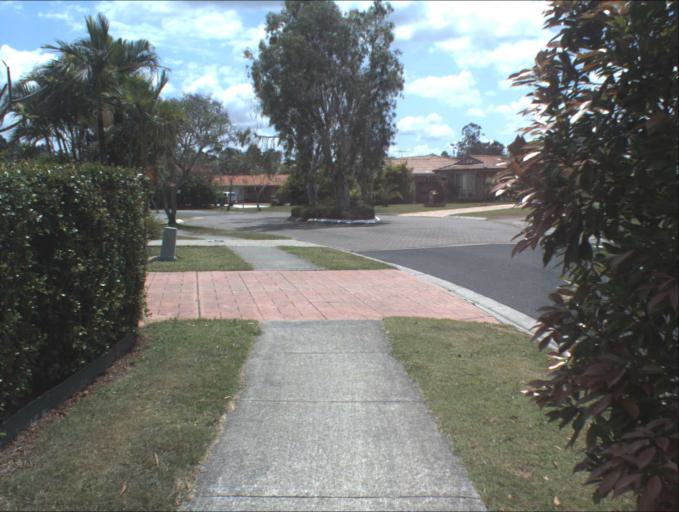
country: AU
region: Queensland
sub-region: Logan
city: Slacks Creek
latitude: -27.6687
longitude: 153.1516
